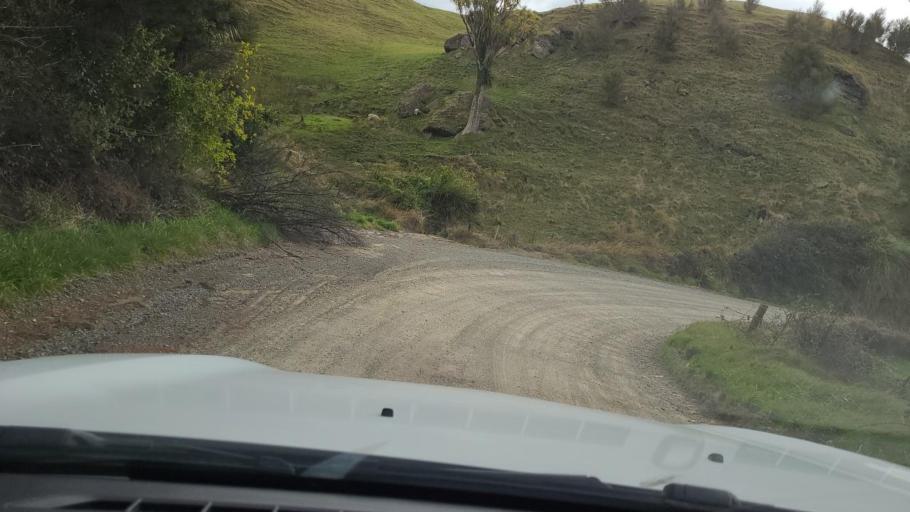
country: NZ
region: Hawke's Bay
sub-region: Napier City
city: Napier
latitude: -39.2956
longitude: 176.8332
